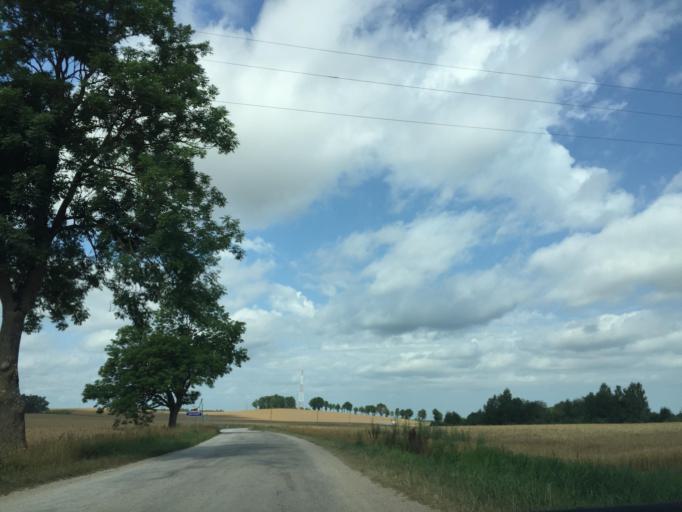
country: LV
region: Kandava
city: Kandava
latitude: 56.9730
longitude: 22.9276
